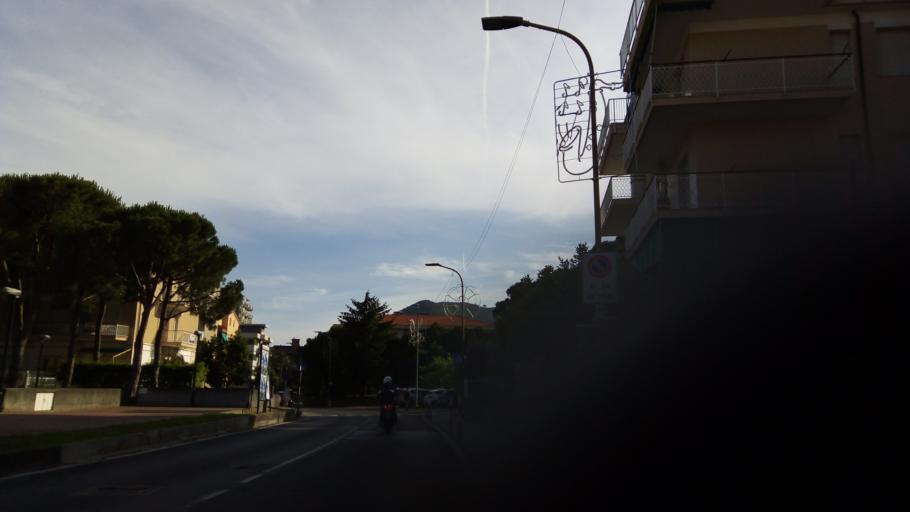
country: IT
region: Liguria
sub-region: Provincia di Savona
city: Borghetto Santo Spirito
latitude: 44.1198
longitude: 8.2486
